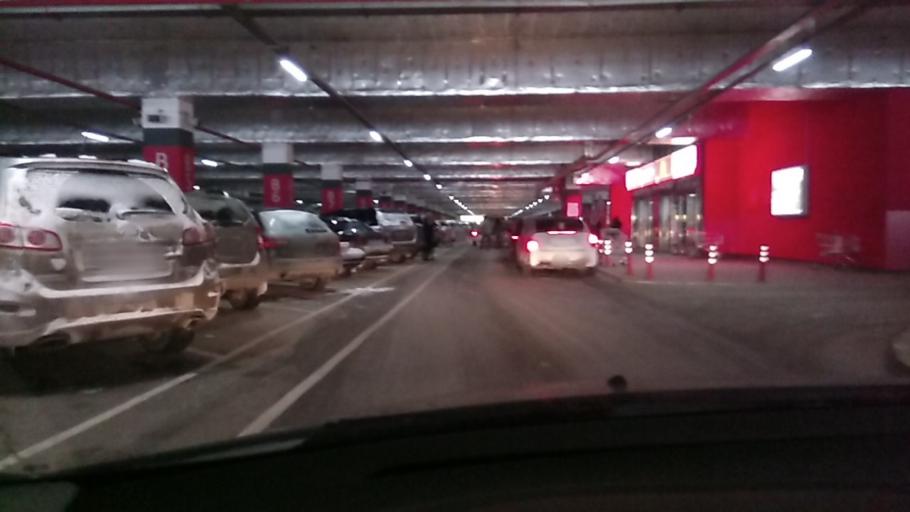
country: RU
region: Sverdlovsk
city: Sovkhoznyy
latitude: 56.8180
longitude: 60.5394
